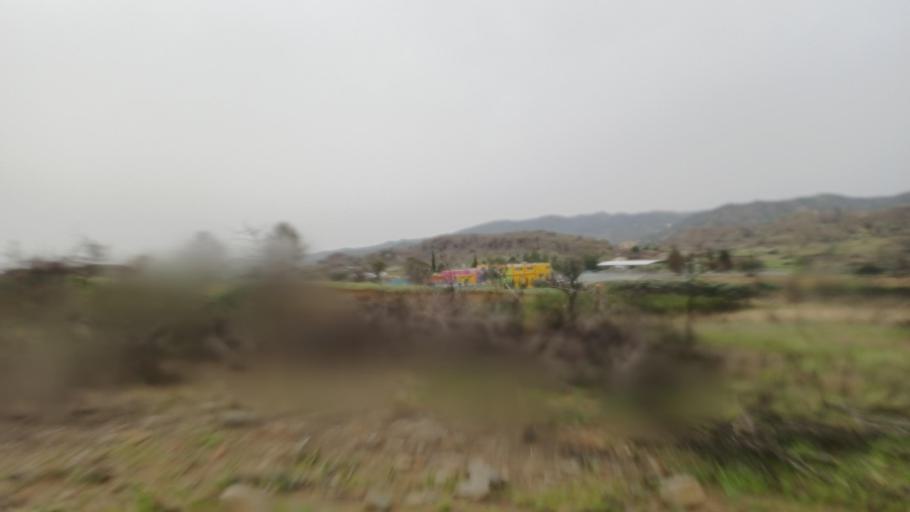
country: CY
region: Limassol
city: Parekklisha
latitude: 34.8489
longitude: 33.1418
